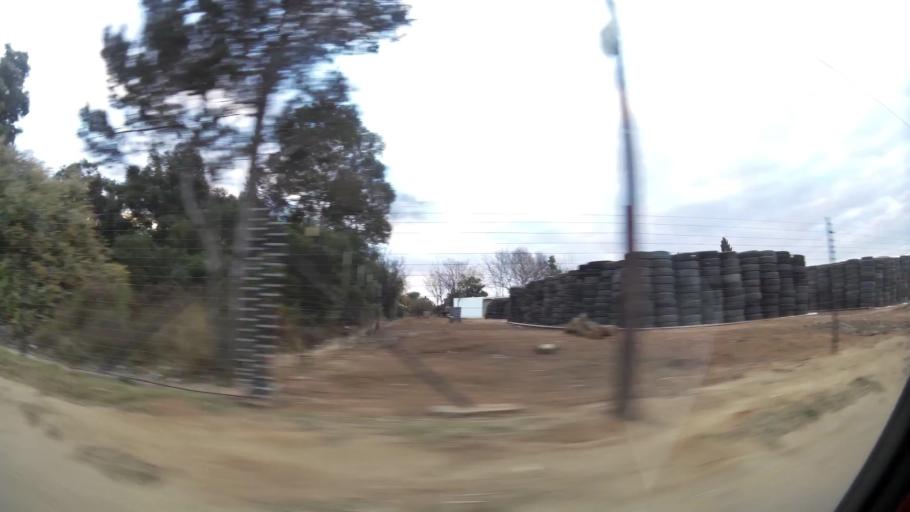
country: ZA
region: Gauteng
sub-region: City of Johannesburg Metropolitan Municipality
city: Midrand
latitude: -25.9836
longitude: 28.1603
